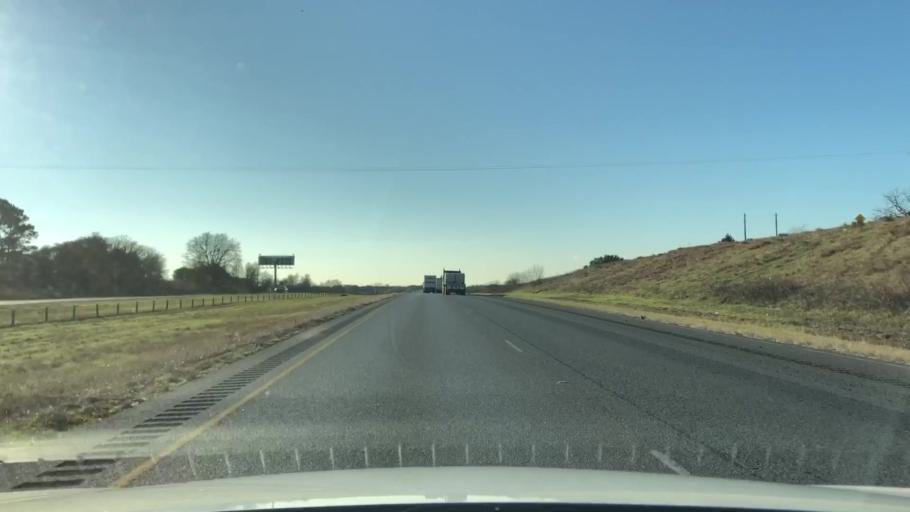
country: US
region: Texas
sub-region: Fayette County
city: Schulenburg
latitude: 29.6903
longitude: -96.9306
